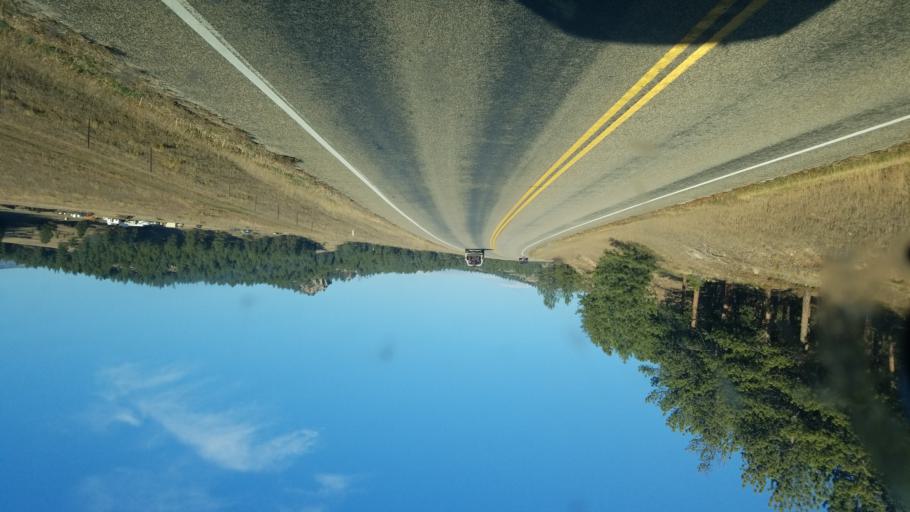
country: US
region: Colorado
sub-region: Teller County
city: Woodland Park
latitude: 38.9966
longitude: -105.3716
